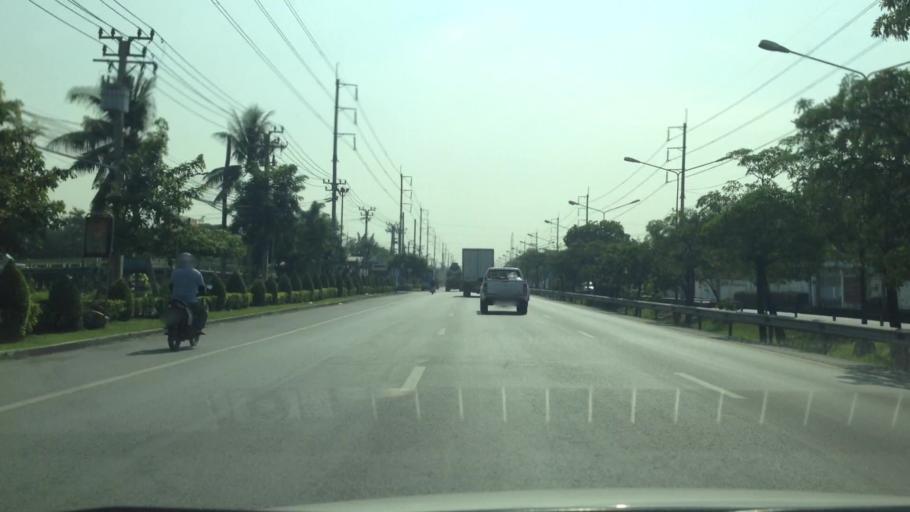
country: TH
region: Samut Prakan
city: Samut Prakan
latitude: 13.5310
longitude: 100.6325
